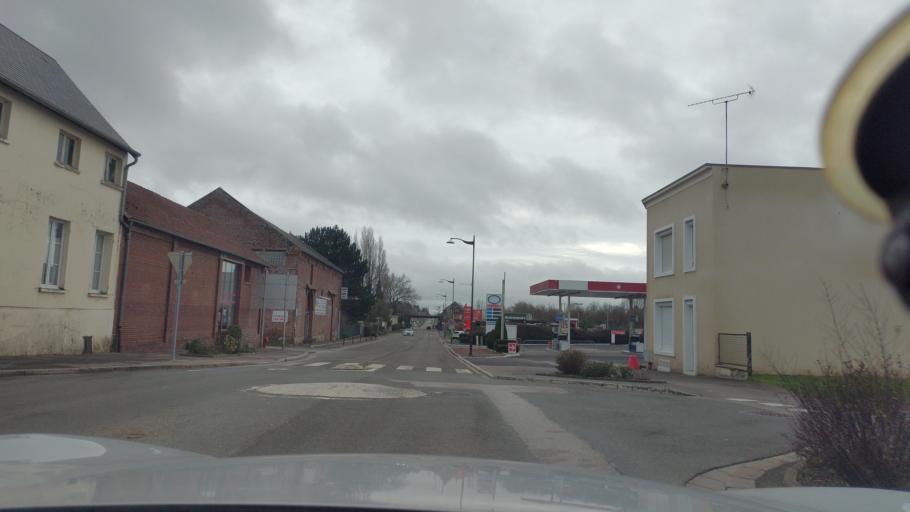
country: FR
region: Picardie
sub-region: Departement de l'Oise
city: Grandvilliers
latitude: 49.6617
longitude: 1.9406
